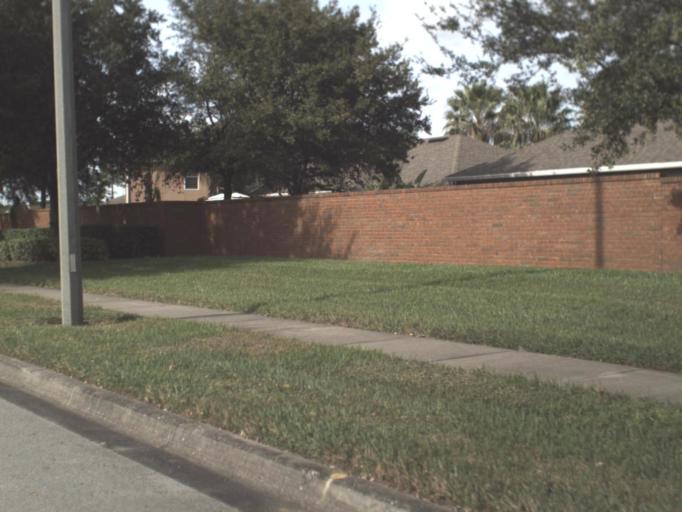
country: US
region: Florida
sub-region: Orange County
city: Conway
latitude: 28.4241
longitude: -81.2502
